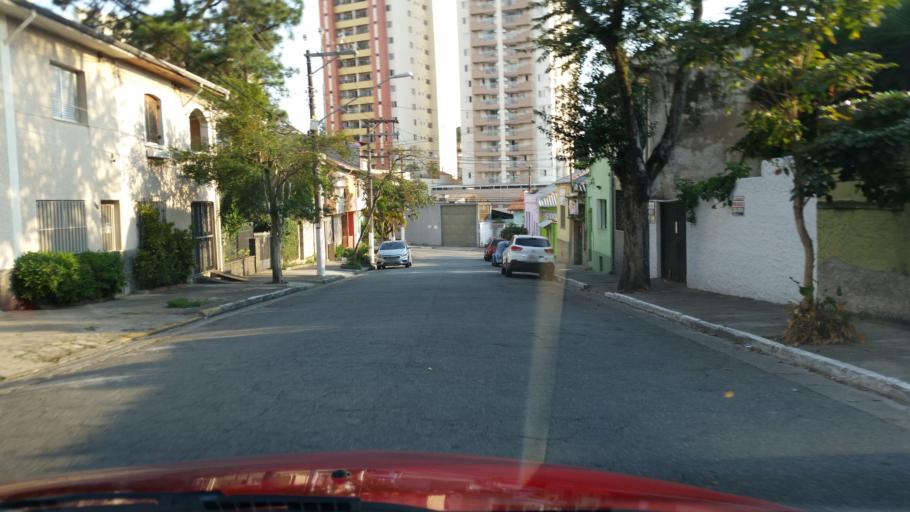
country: BR
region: Sao Paulo
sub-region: Sao Paulo
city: Sao Paulo
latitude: -23.6035
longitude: -46.6231
